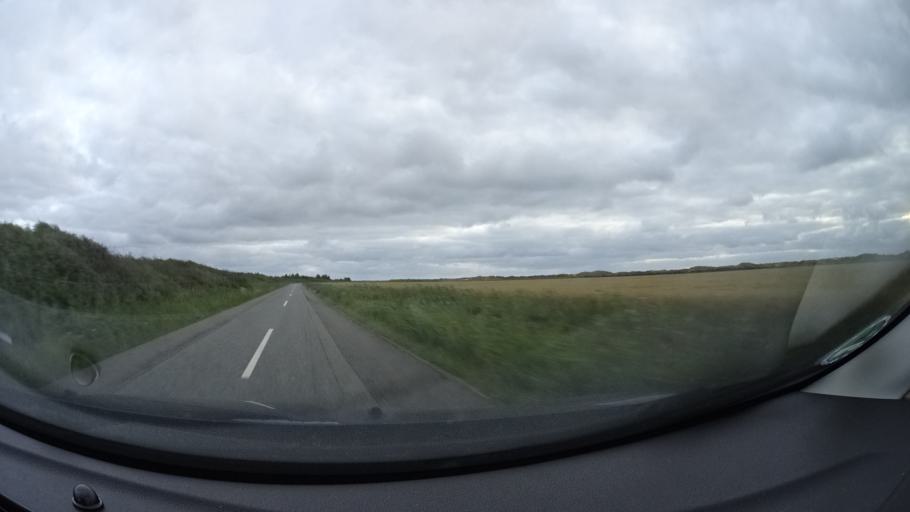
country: DK
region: Central Jutland
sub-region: Ringkobing-Skjern Kommune
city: Ringkobing
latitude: 56.1544
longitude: 8.1388
